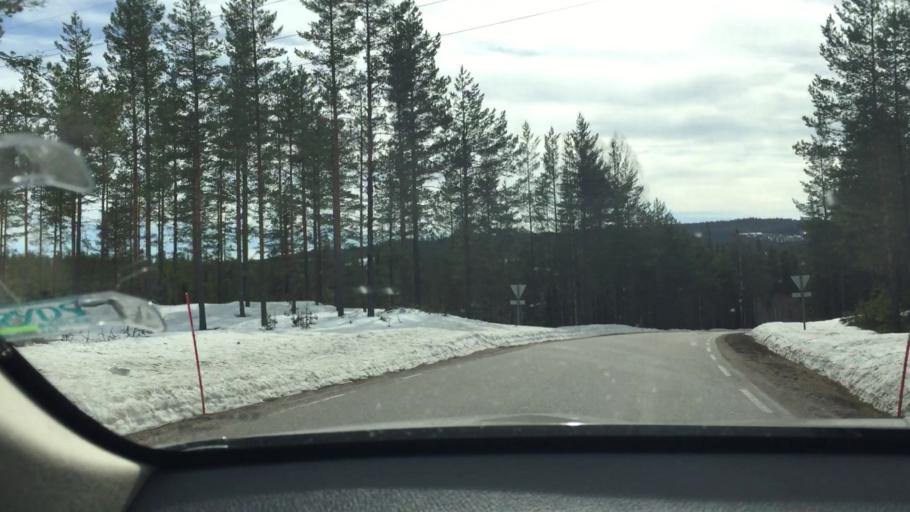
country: NO
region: Hedmark
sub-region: Trysil
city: Innbygda
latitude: 61.0733
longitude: 12.5710
